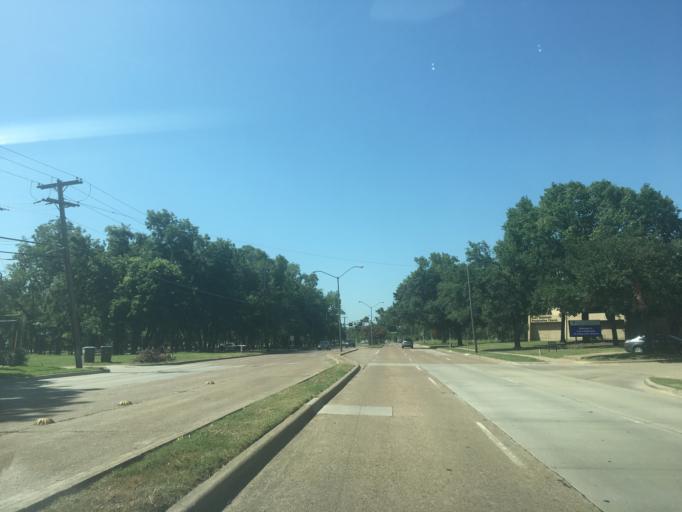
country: US
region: Texas
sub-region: Dallas County
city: Highland Park
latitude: 32.8655
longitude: -96.7179
